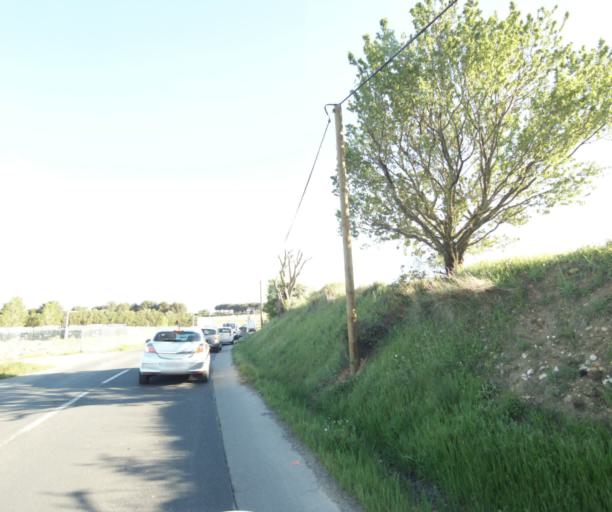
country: FR
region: Languedoc-Roussillon
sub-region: Departement de l'Herault
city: Lattes
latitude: 43.5779
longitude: 3.9224
